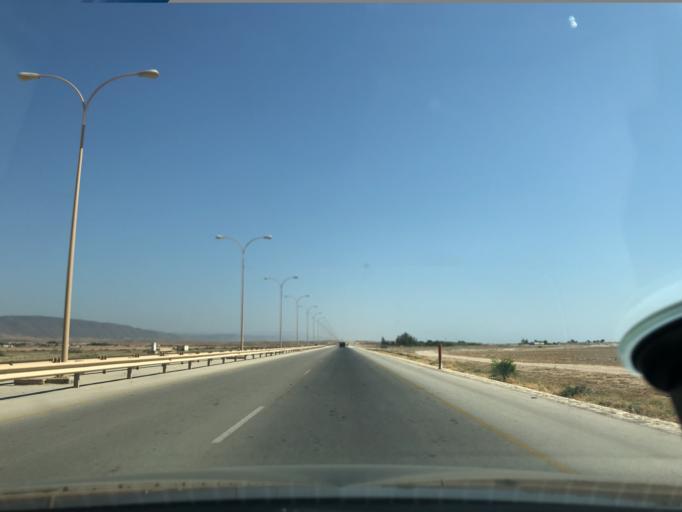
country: OM
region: Zufar
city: Salalah
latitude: 17.0525
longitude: 54.2882
